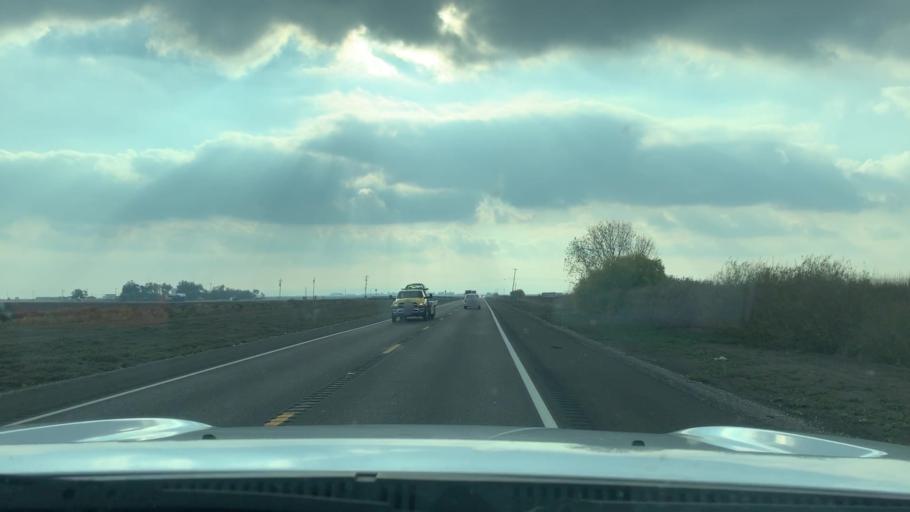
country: US
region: California
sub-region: Kings County
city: Stratford
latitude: 36.1630
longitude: -119.8492
